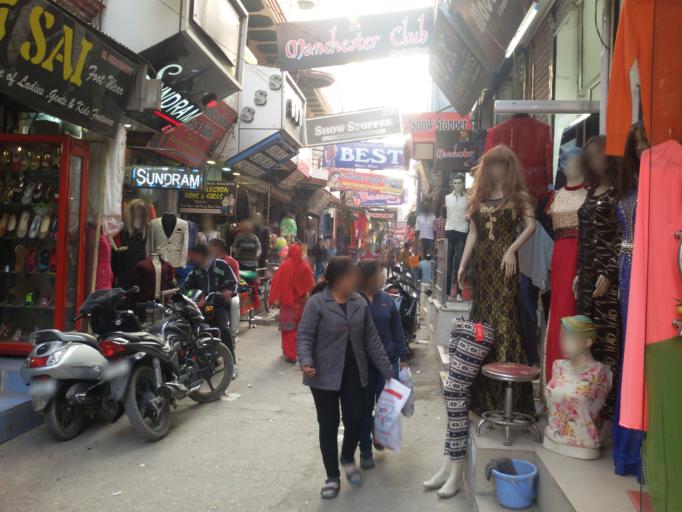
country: IN
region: Haryana
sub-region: Sonipat
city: Sonipat
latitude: 28.9904
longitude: 77.0250
